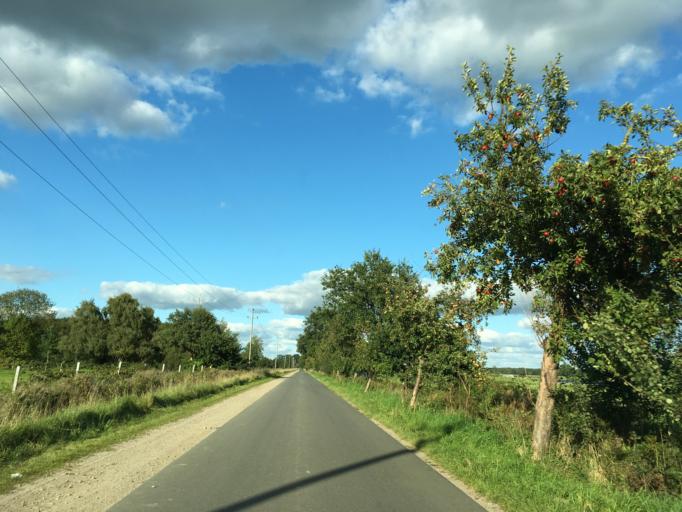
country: DE
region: Lower Saxony
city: Salzhausen
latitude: 53.2361
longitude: 10.1774
